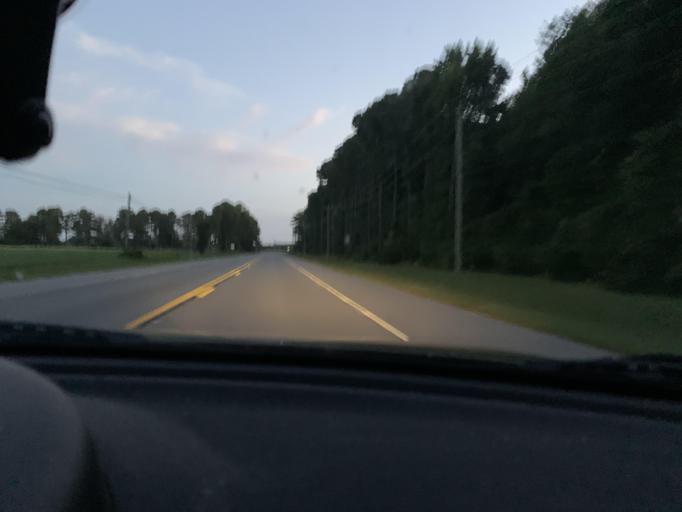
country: US
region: Maryland
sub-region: Talbot County
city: Saint Michaels
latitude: 38.7559
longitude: -76.3196
